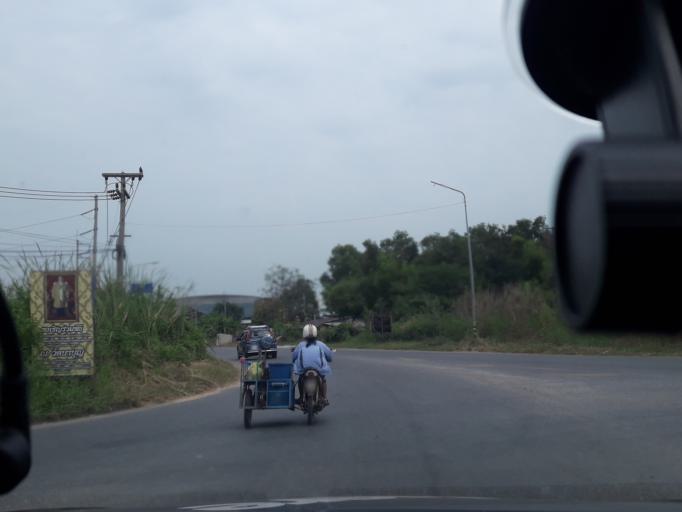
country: TH
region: Pathum Thani
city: Ban Rangsit
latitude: 14.0129
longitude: 100.7529
